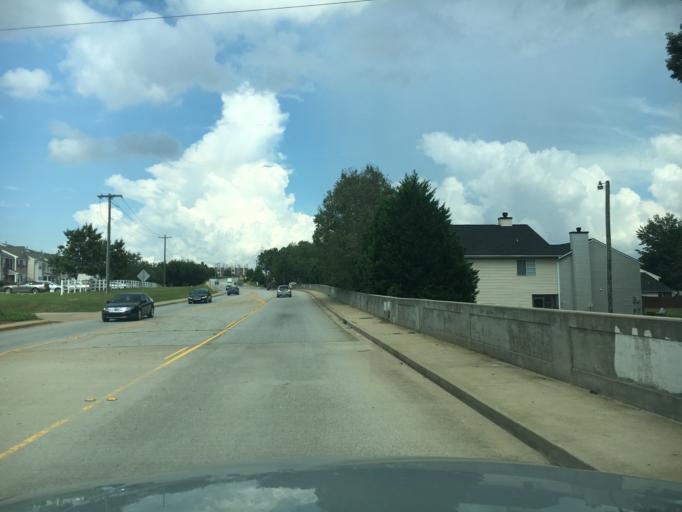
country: US
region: South Carolina
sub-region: Greenville County
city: Taylors
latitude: 34.8974
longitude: -82.2612
